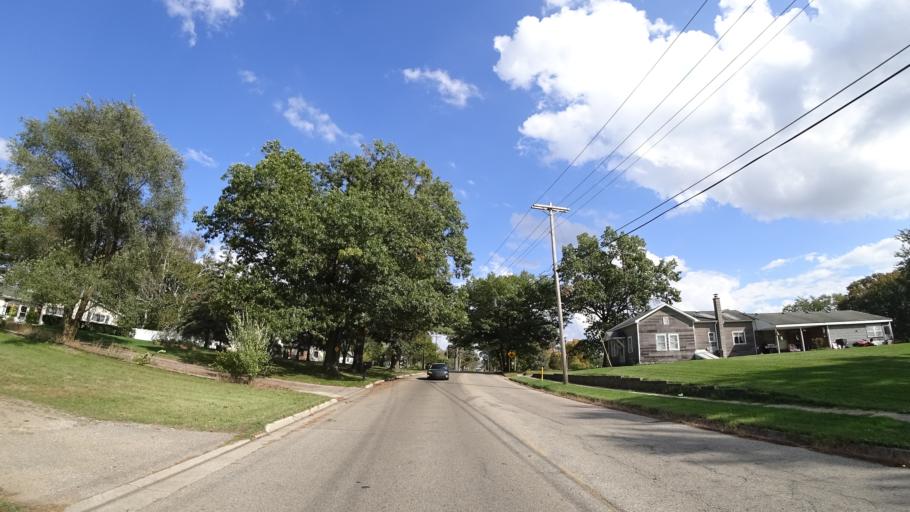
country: US
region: Michigan
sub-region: Saint Joseph County
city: Three Rivers
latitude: 41.9547
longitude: -85.6206
